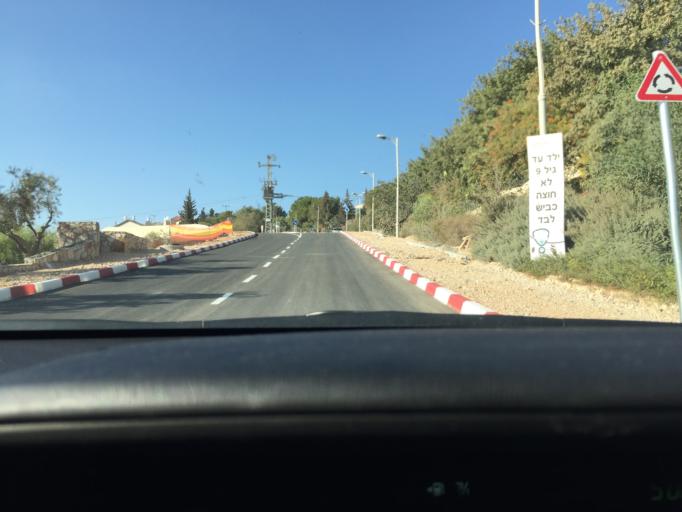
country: PS
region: West Bank
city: Al Lubban al Gharbi
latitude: 32.0330
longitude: 35.0502
